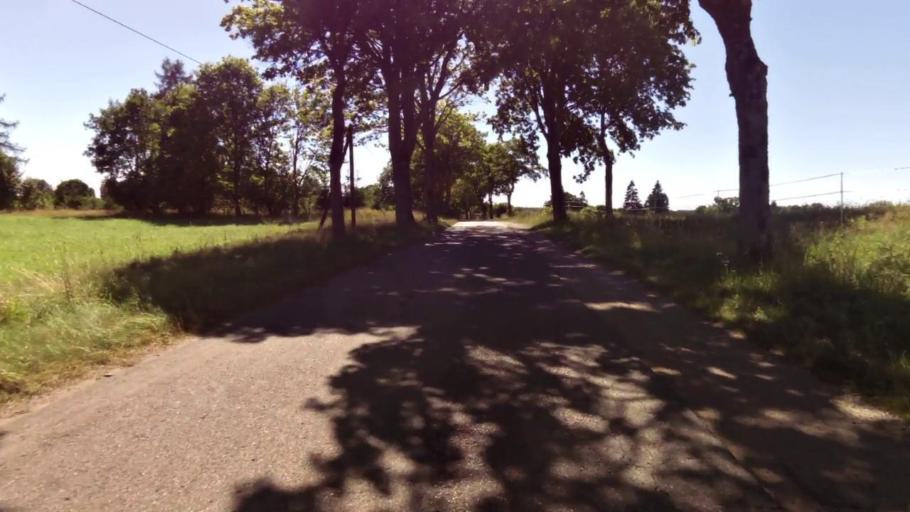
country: PL
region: West Pomeranian Voivodeship
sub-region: Powiat szczecinecki
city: Bialy Bor
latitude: 53.8774
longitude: 16.7997
